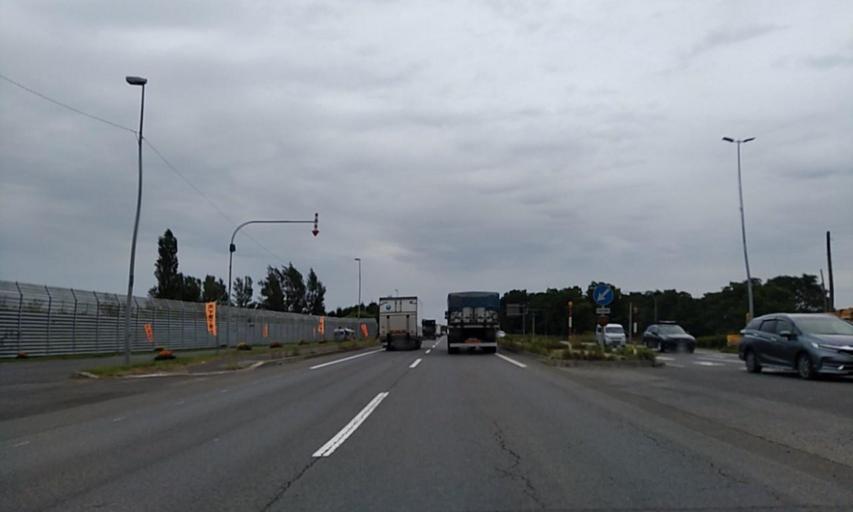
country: JP
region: Hokkaido
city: Sapporo
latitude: 43.1529
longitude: 141.2389
